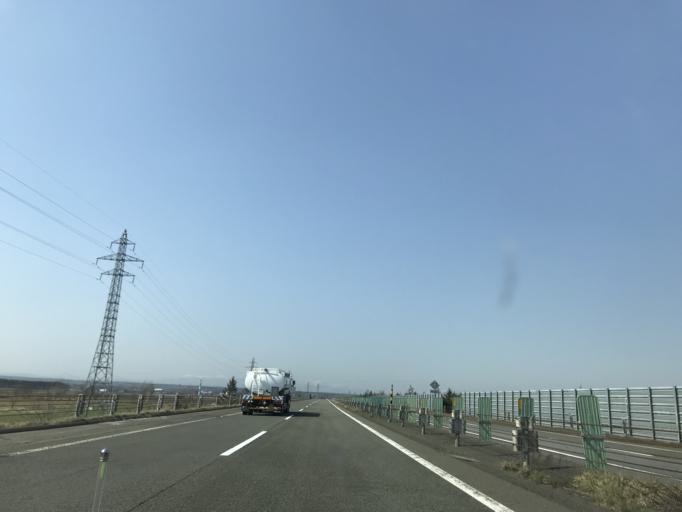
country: JP
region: Hokkaido
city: Ebetsu
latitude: 43.0902
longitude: 141.5715
